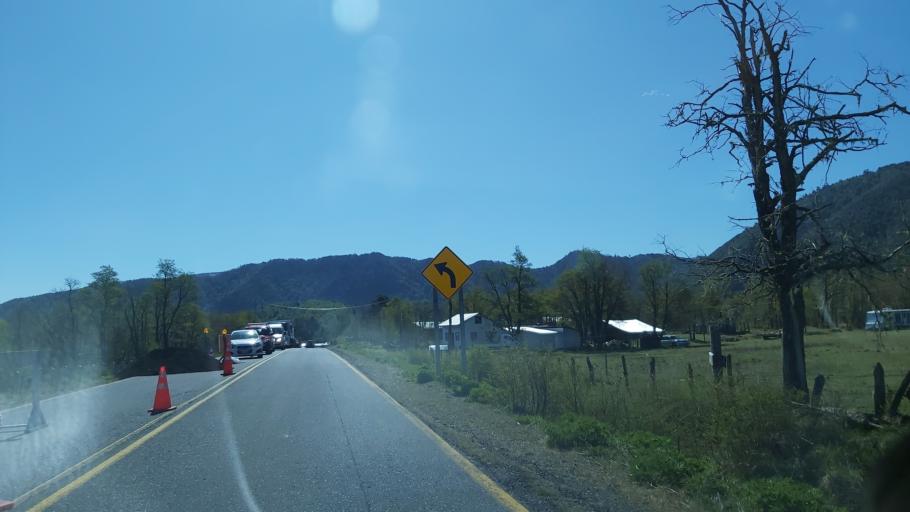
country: CL
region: Araucania
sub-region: Provincia de Cautin
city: Vilcun
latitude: -38.4657
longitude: -71.6049
